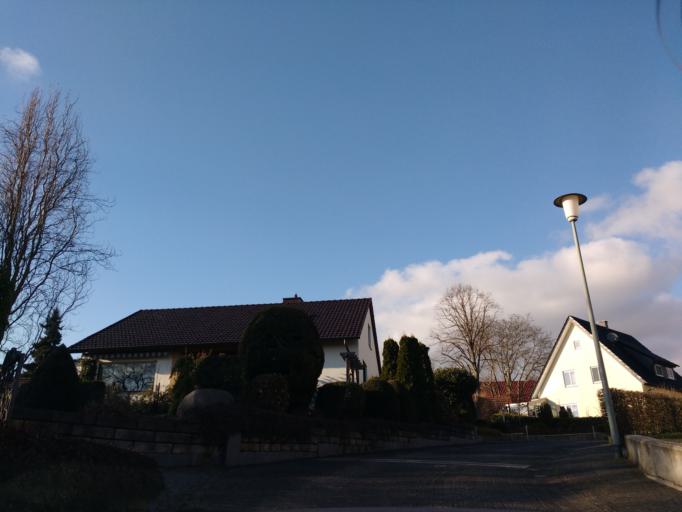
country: DE
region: North Rhine-Westphalia
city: Bad Lippspringe
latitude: 51.7479
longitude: 8.8493
